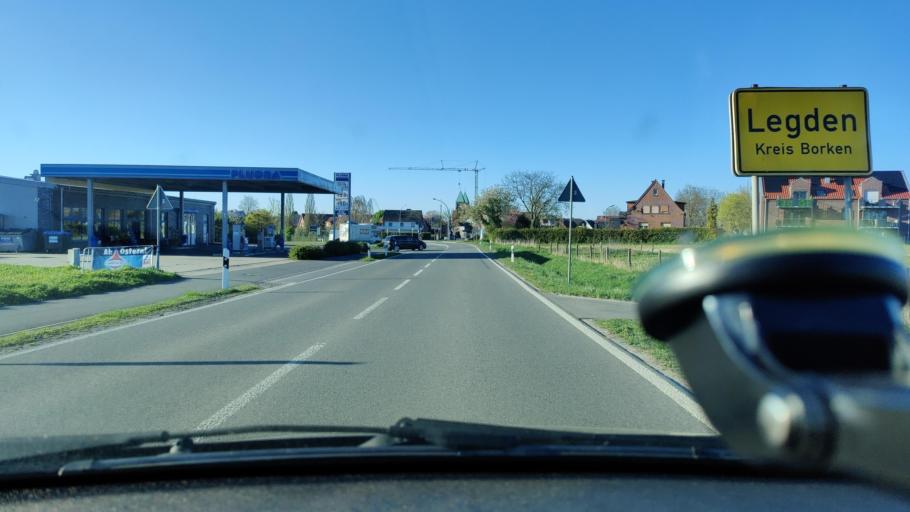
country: DE
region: North Rhine-Westphalia
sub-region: Regierungsbezirk Munster
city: Legden
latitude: 52.0259
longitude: 7.1056
